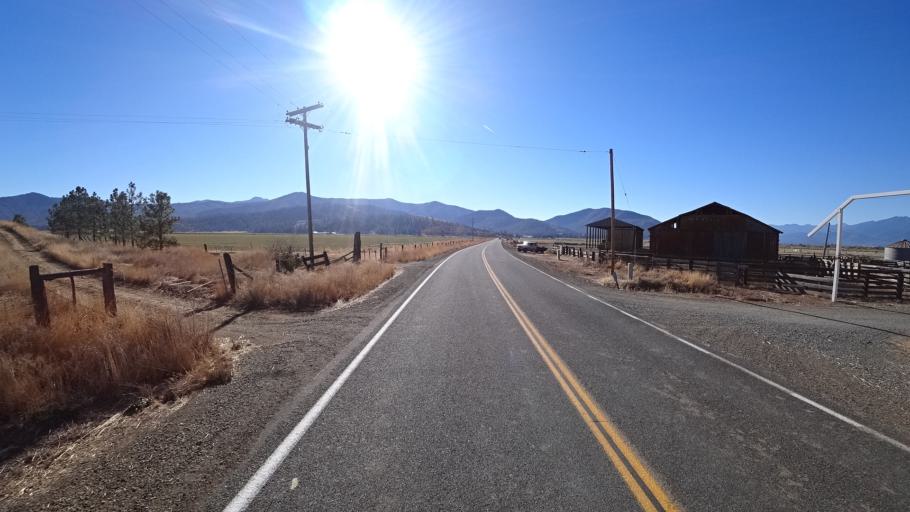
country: US
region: California
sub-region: Siskiyou County
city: Yreka
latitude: 41.5689
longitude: -122.8348
